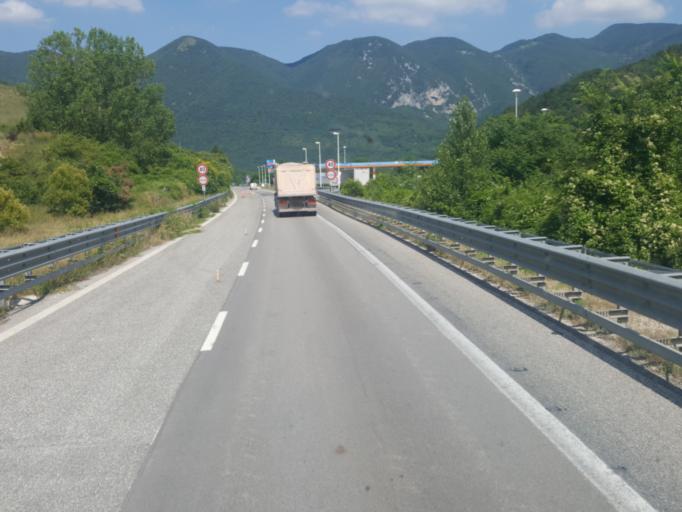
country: IT
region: The Marches
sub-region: Provincia di Ancona
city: Cerreto d'Esi
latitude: 43.3441
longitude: 12.9781
